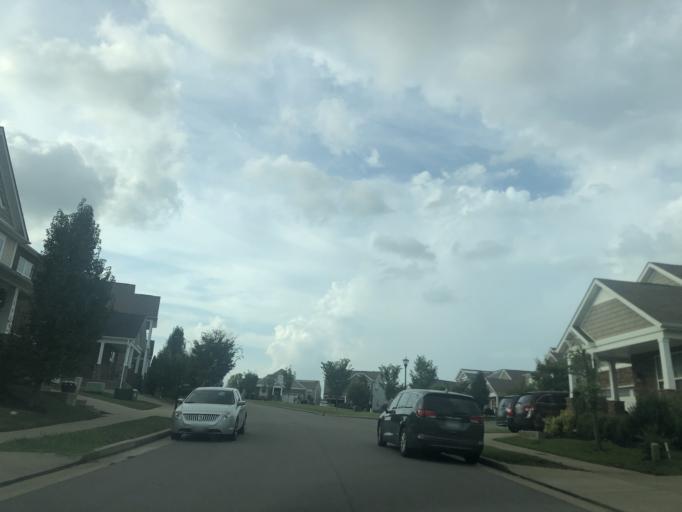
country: US
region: Tennessee
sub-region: Davidson County
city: Lakewood
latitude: 36.1664
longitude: -86.6202
